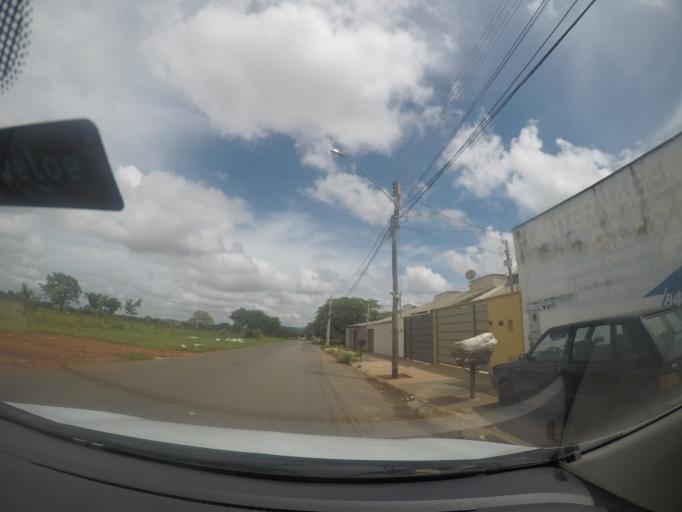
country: BR
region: Goias
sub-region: Goiania
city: Goiania
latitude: -16.7057
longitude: -49.3308
